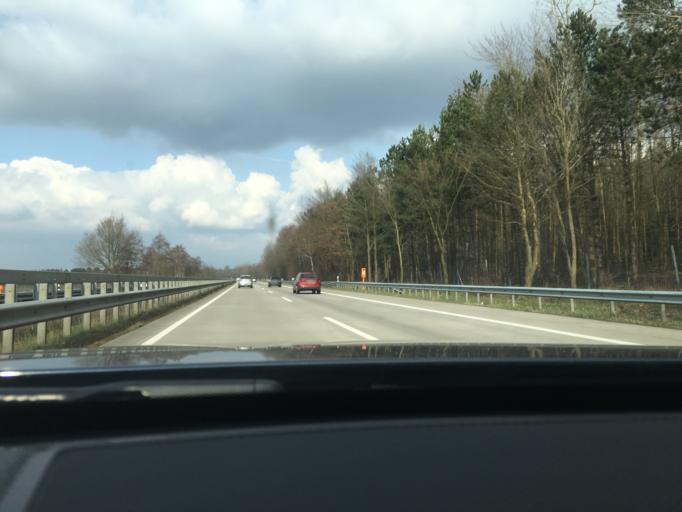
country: DE
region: Lower Saxony
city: Schwanewede
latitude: 53.2624
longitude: 8.6359
